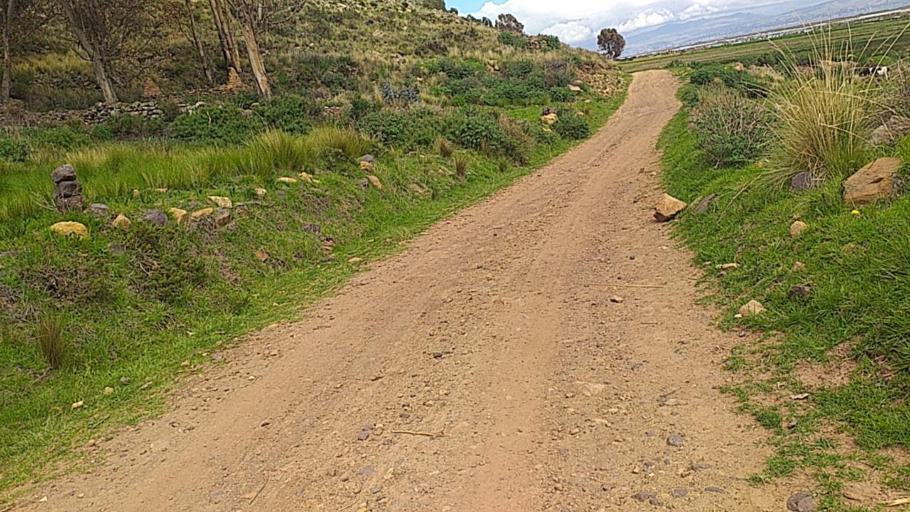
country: BO
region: La Paz
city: Batallas
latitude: -16.3309
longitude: -68.6398
